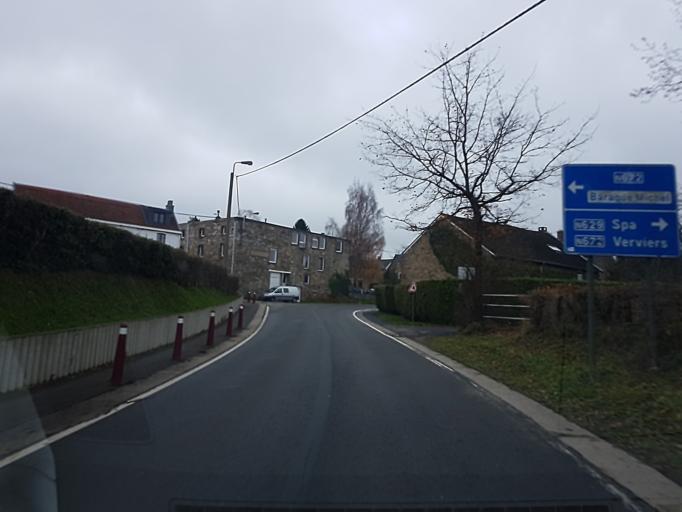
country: BE
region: Wallonia
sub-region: Province de Liege
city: Jalhay
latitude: 50.5606
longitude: 5.9666
